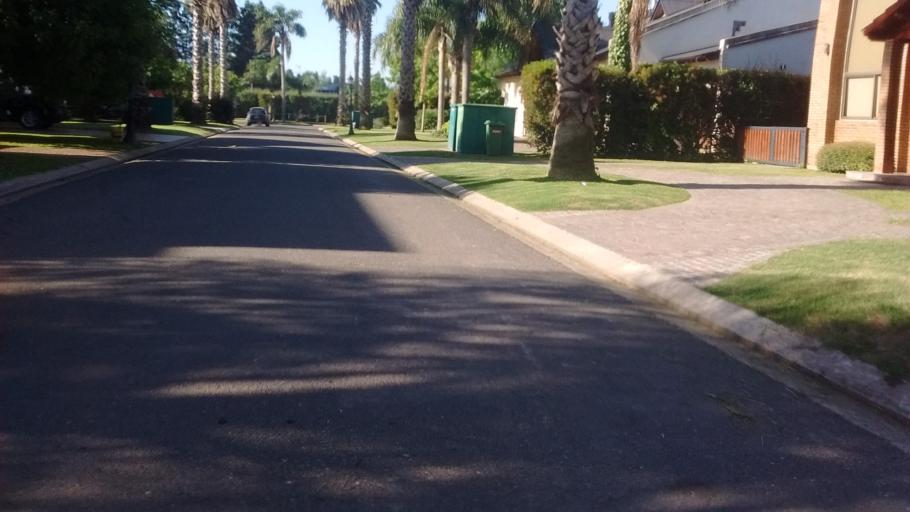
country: AR
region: Santa Fe
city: Funes
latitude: -32.9249
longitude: -60.8213
